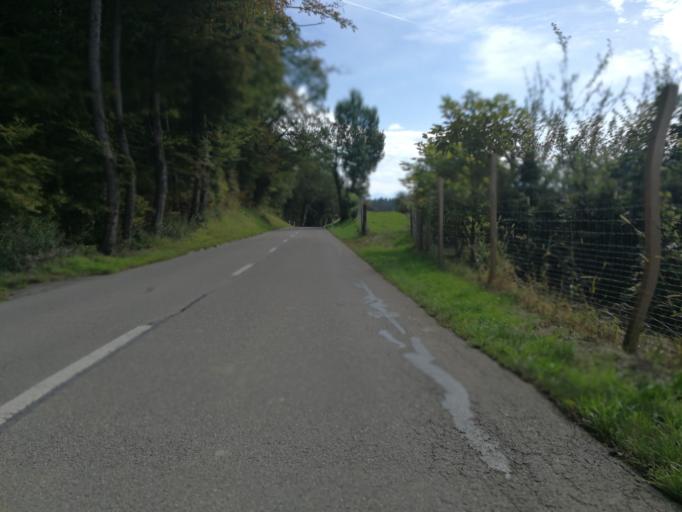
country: CH
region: Zurich
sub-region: Bezirk Meilen
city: Uetikon / Grossdorf
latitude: 47.2774
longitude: 8.6914
